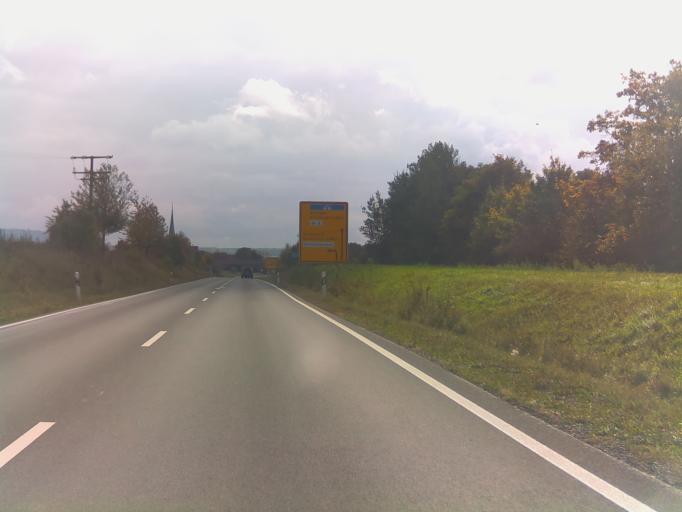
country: DE
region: Bavaria
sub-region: Regierungsbezirk Unterfranken
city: Sommerach
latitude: 49.8204
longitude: 10.2225
